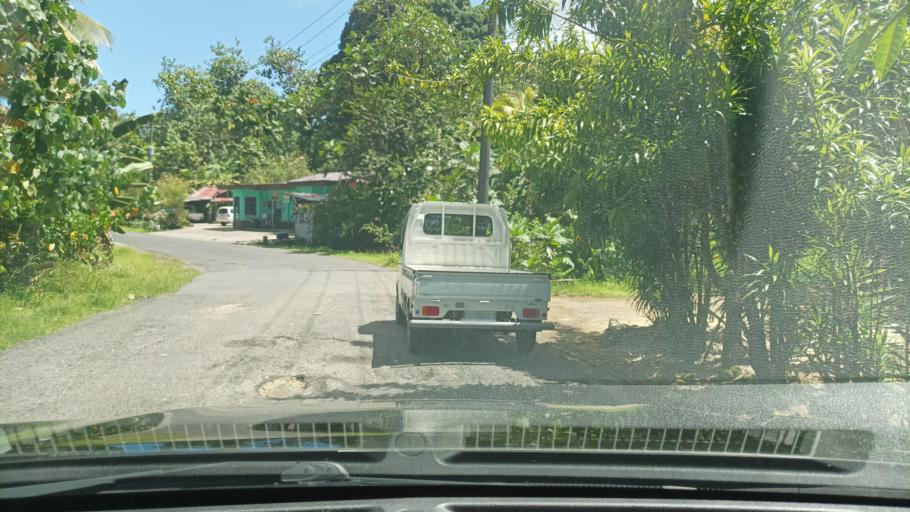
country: FM
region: Pohnpei
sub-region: Kolonia Municipality
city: Kolonia
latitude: 6.9328
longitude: 158.2777
